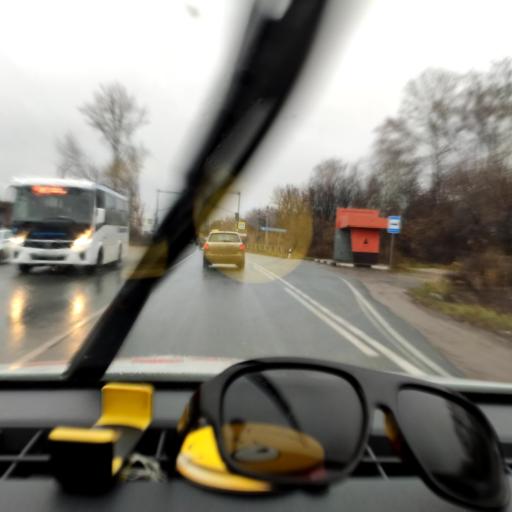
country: RU
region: Bashkortostan
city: Iglino
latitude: 54.7965
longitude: 56.3052
